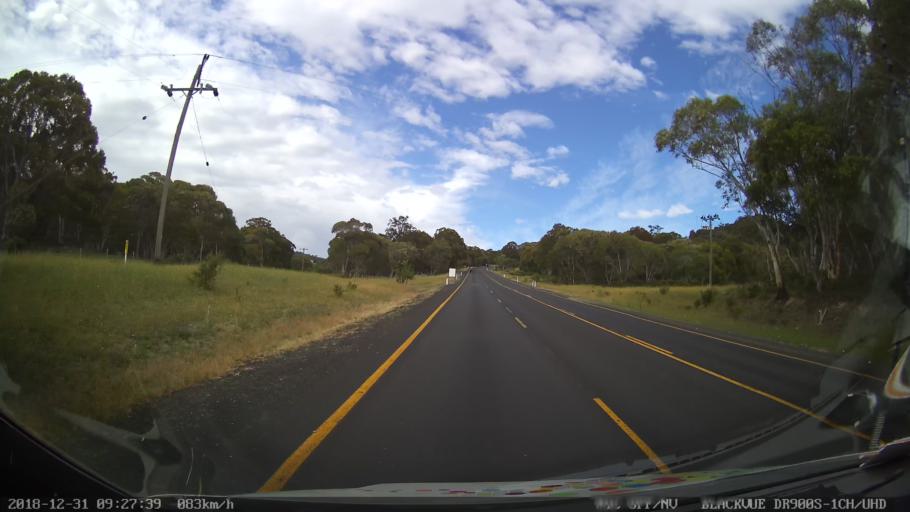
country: AU
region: New South Wales
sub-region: Snowy River
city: Jindabyne
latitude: -36.4577
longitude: 148.4820
